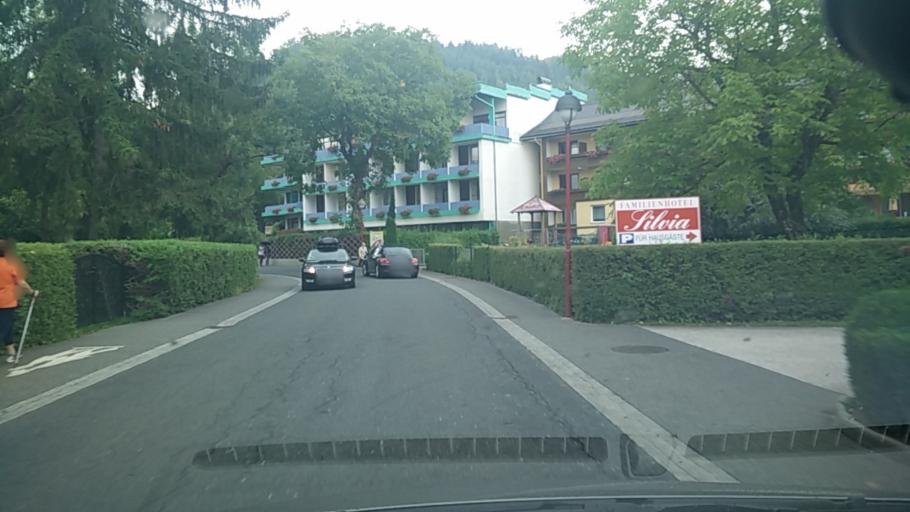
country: AT
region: Carinthia
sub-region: Politischer Bezirk Volkermarkt
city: Sittersdorf
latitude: 46.6056
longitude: 14.5725
